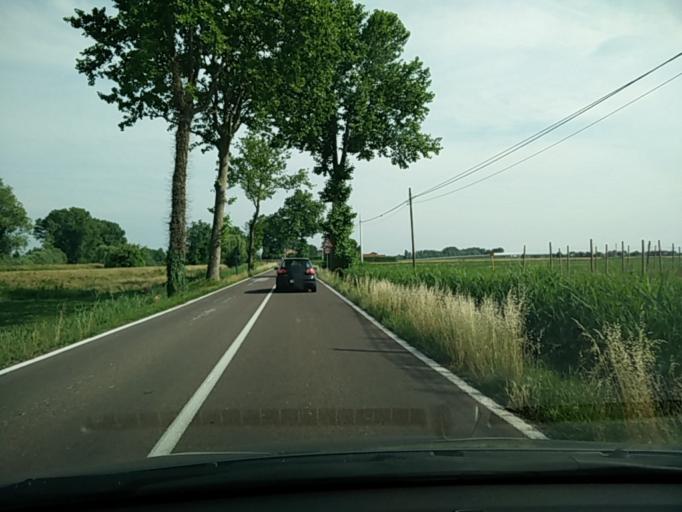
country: IT
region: Veneto
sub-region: Provincia di Venezia
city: Quarto d'Altino
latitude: 45.5761
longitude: 12.3814
